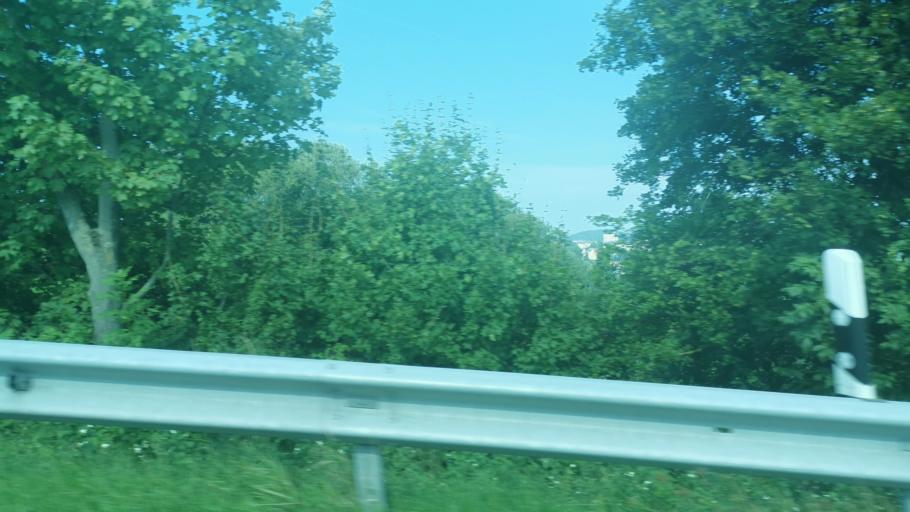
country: DE
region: Bavaria
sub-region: Upper Palatinate
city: Cham
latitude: 49.2144
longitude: 12.6771
